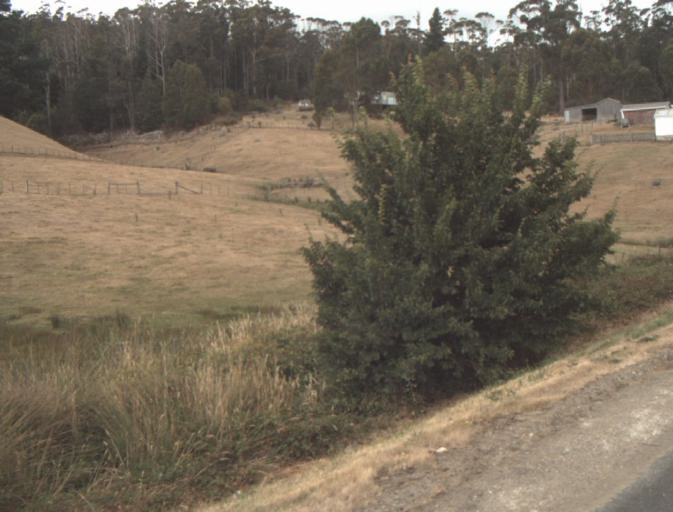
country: AU
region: Tasmania
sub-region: Launceston
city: Mayfield
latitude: -41.2625
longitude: 147.2177
